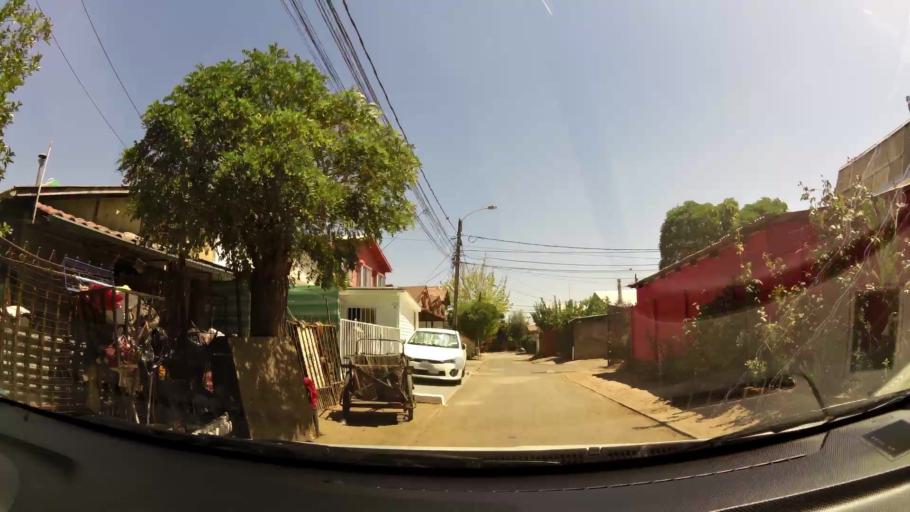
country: CL
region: Maule
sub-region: Provincia de Talca
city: Talca
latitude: -35.4322
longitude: -71.6313
